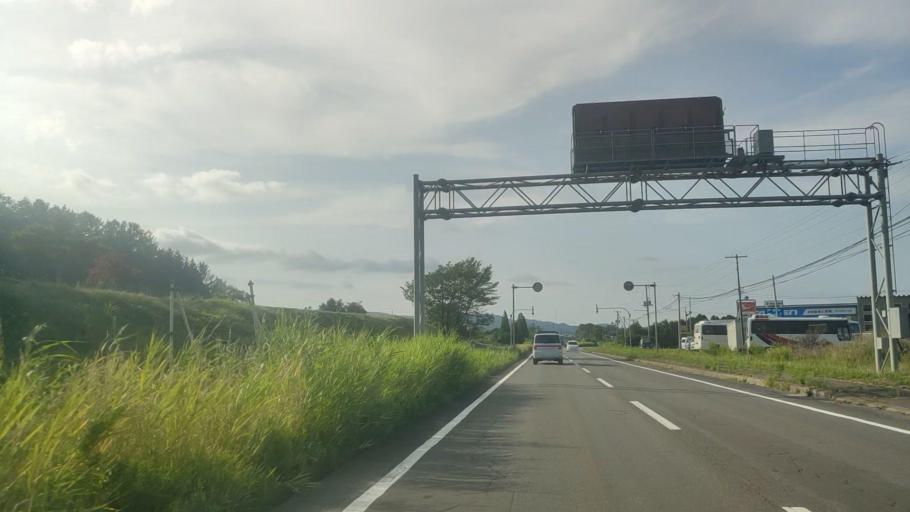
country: JP
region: Hokkaido
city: Chitose
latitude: 42.9532
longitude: 141.8005
